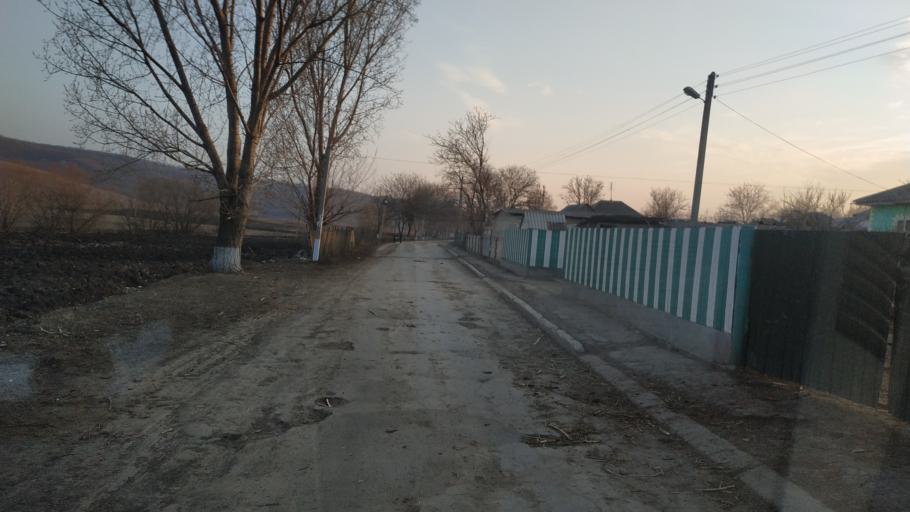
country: MD
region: Hincesti
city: Dancu
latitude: 46.7077
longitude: 28.3451
